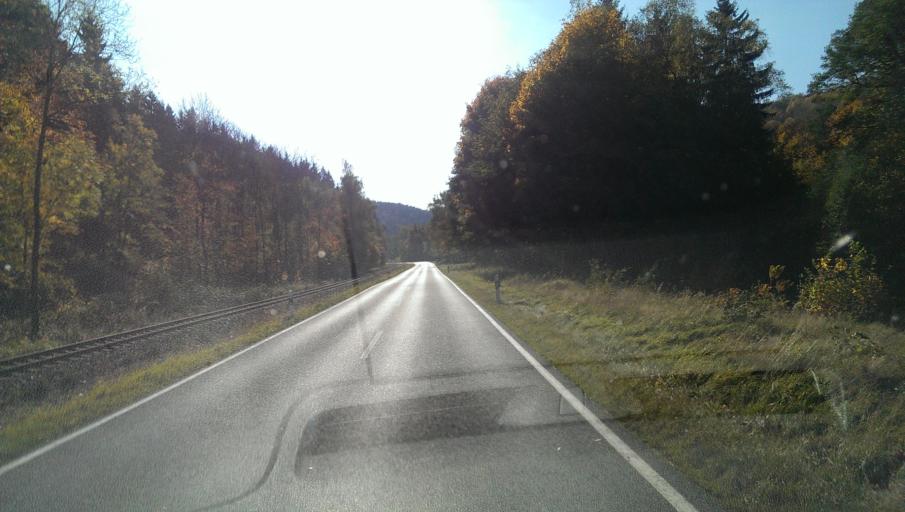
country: DE
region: Saxony
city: Geising
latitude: 50.7751
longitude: 13.7914
